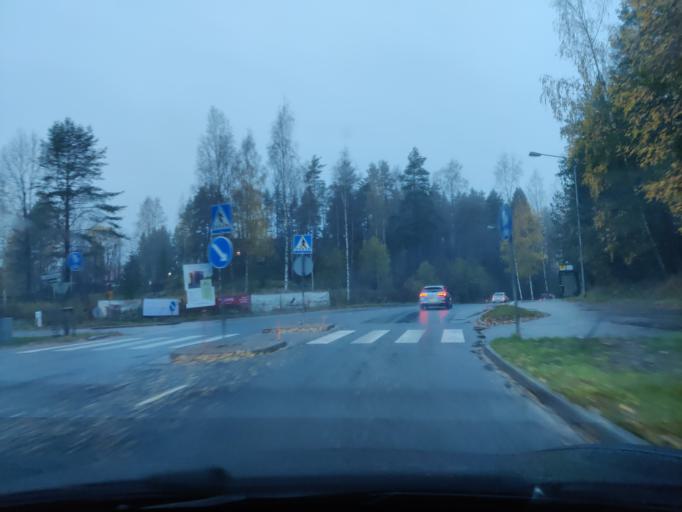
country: FI
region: Northern Savo
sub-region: Kuopio
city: Kuopio
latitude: 62.8480
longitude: 27.6421
